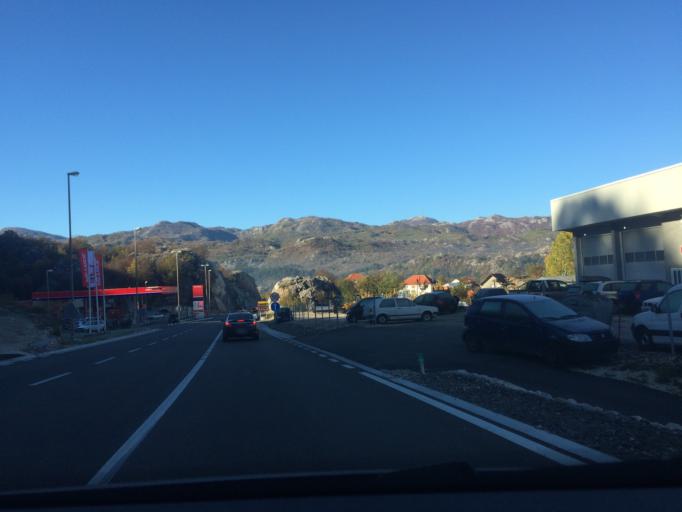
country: ME
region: Cetinje
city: Cetinje
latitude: 42.3883
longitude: 18.9347
